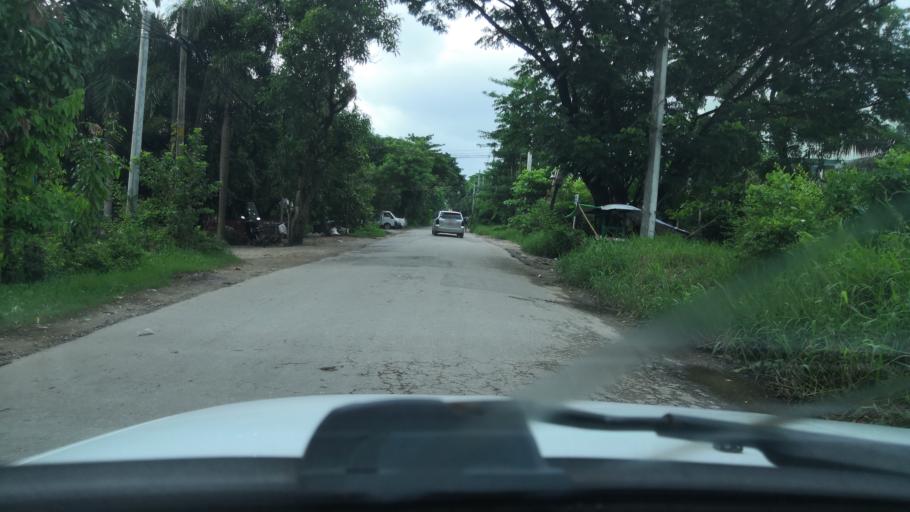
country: MM
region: Yangon
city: Yangon
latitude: 16.8810
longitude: 96.1795
